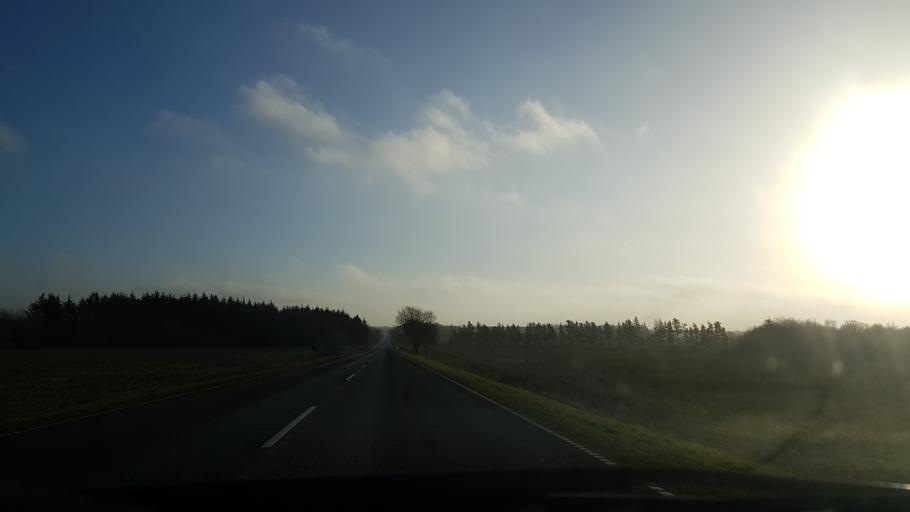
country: DK
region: South Denmark
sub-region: Tonder Kommune
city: Toftlund
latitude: 55.2138
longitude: 9.1855
